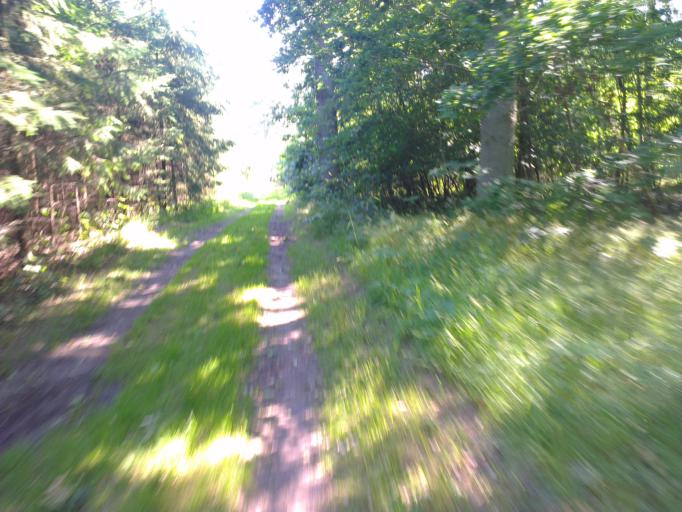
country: DK
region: Capital Region
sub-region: Frederikssund Kommune
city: Skibby
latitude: 55.7975
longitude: 11.8769
